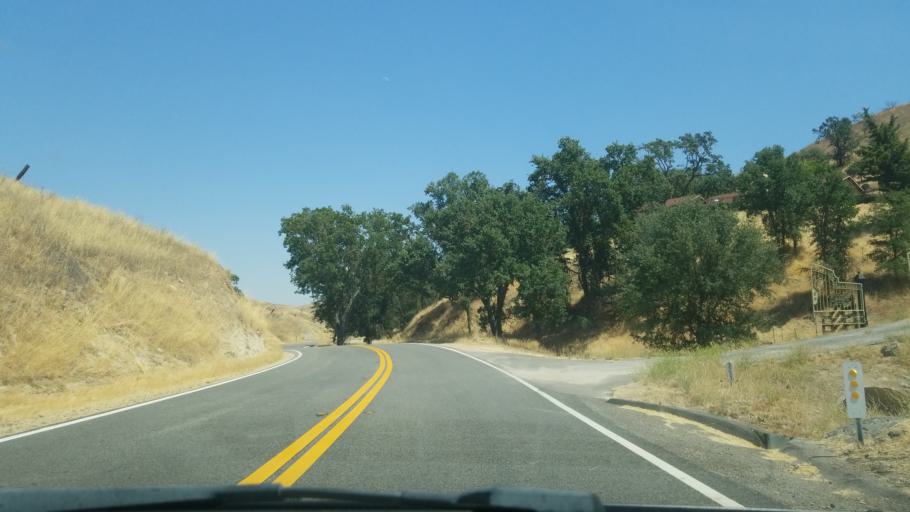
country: US
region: California
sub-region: San Luis Obispo County
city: Shandon
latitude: 35.5793
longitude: -120.4518
